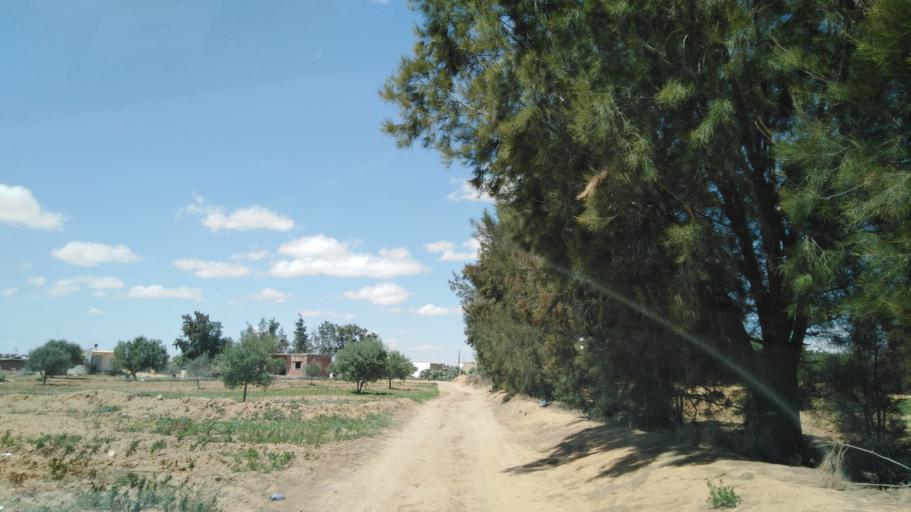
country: TN
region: Safaqis
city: Sfax
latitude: 34.7468
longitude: 10.5404
